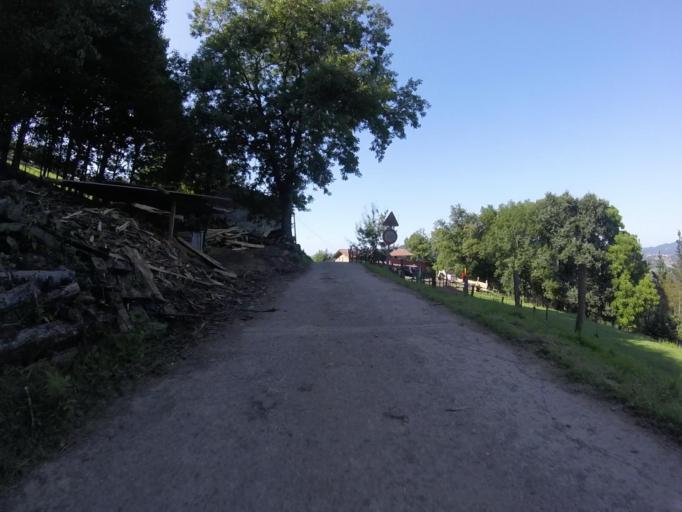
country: ES
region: Basque Country
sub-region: Provincia de Guipuzcoa
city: Astigarraga
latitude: 43.2745
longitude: -1.9295
